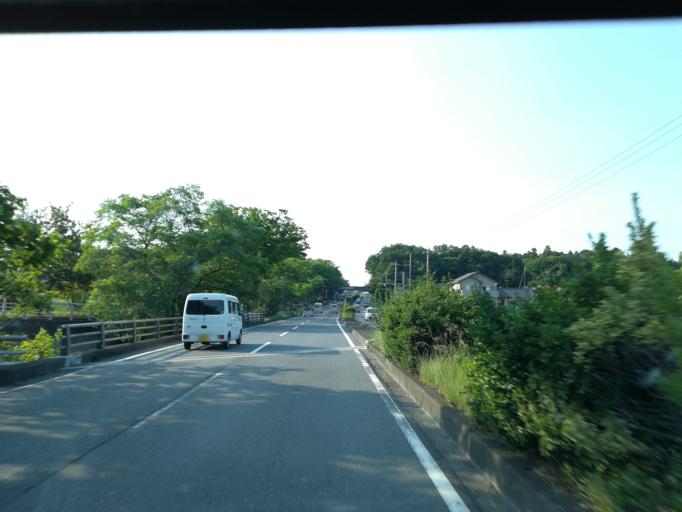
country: JP
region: Saitama
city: Kumagaya
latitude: 36.0497
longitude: 139.3756
